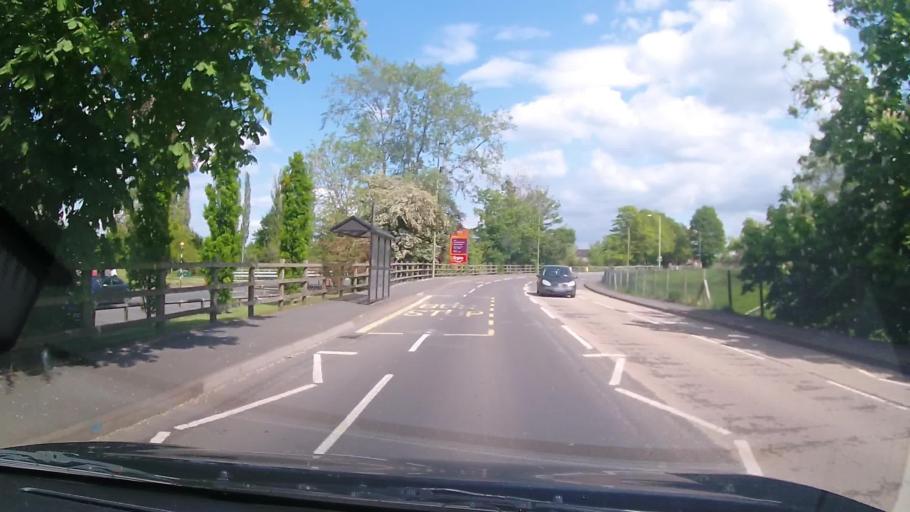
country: GB
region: England
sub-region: Shropshire
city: Whitchurch
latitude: 52.9711
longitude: -2.6868
